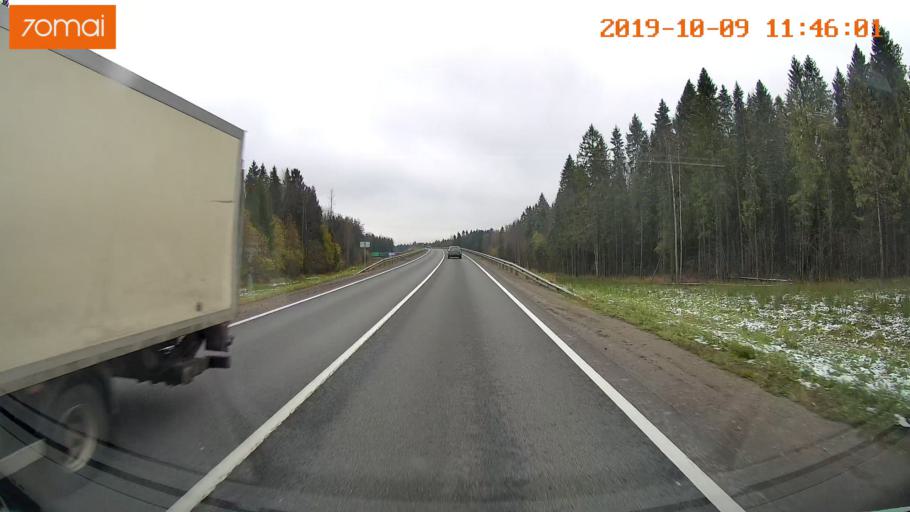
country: RU
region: Vologda
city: Gryazovets
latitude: 58.8601
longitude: 40.1991
